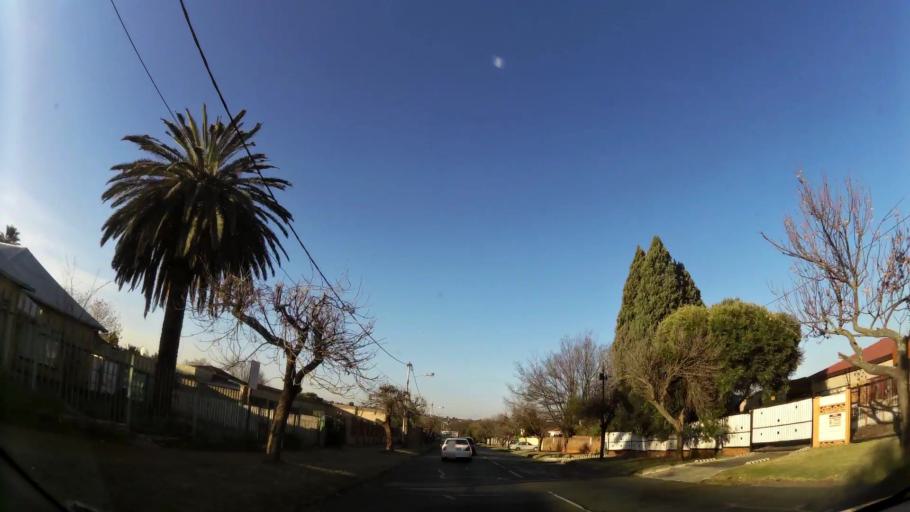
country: ZA
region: Gauteng
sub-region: City of Johannesburg Metropolitan Municipality
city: Roodepoort
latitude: -26.1837
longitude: 27.9237
